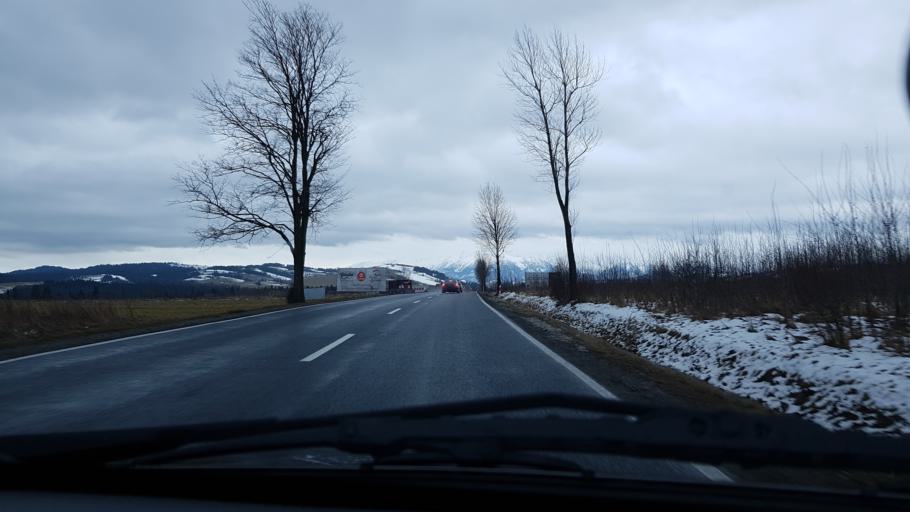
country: PL
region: Lesser Poland Voivodeship
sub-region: Powiat tatrzanski
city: Bialka Tatrzanska
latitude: 49.4155
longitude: 20.0965
